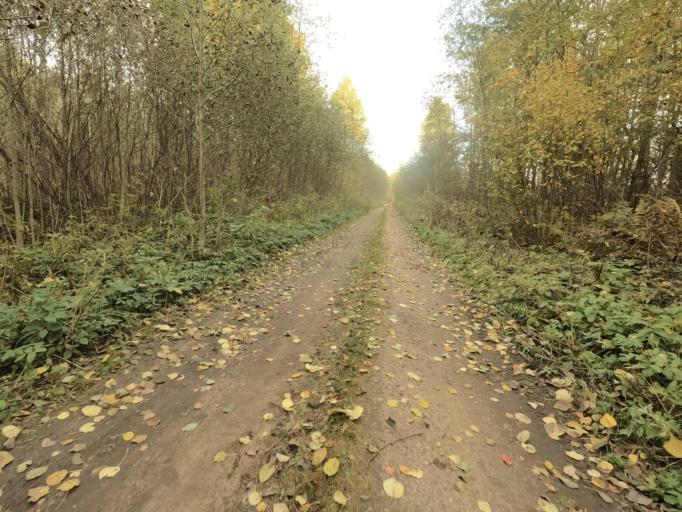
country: RU
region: Novgorod
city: Pankovka
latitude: 58.8802
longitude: 30.8433
